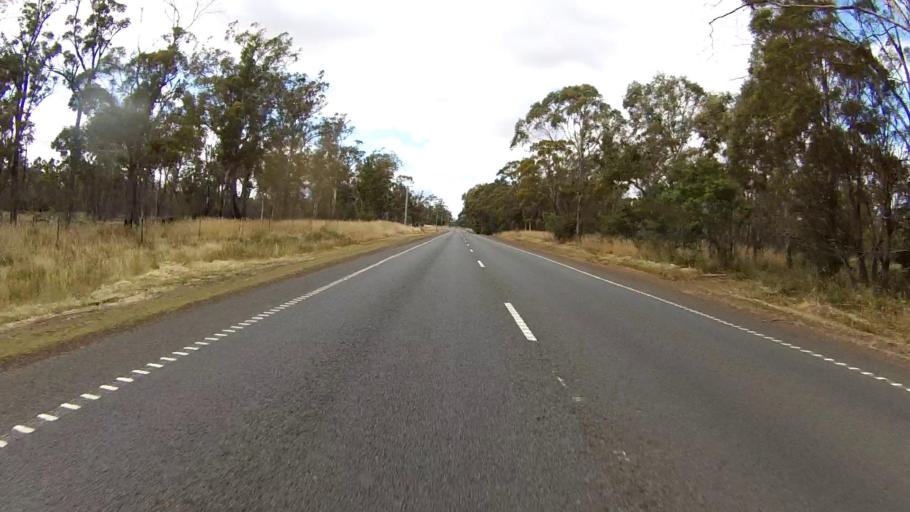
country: AU
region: Tasmania
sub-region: Northern Midlands
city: Evandale
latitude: -41.8234
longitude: 147.4279
